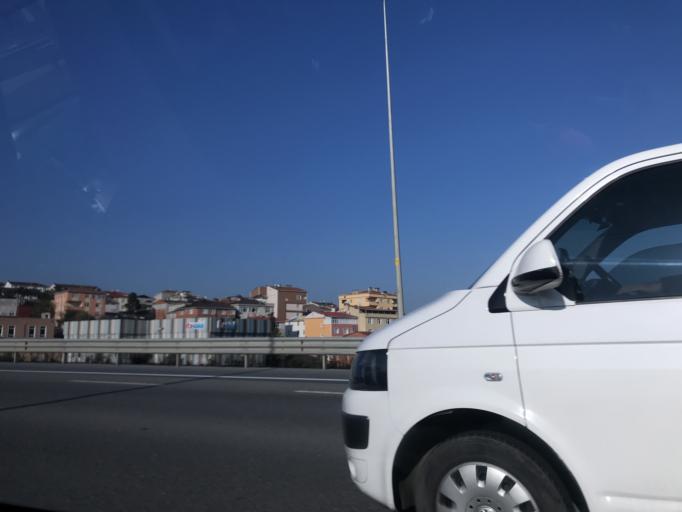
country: TR
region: Istanbul
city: Sultanbeyli
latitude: 40.9510
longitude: 29.3043
